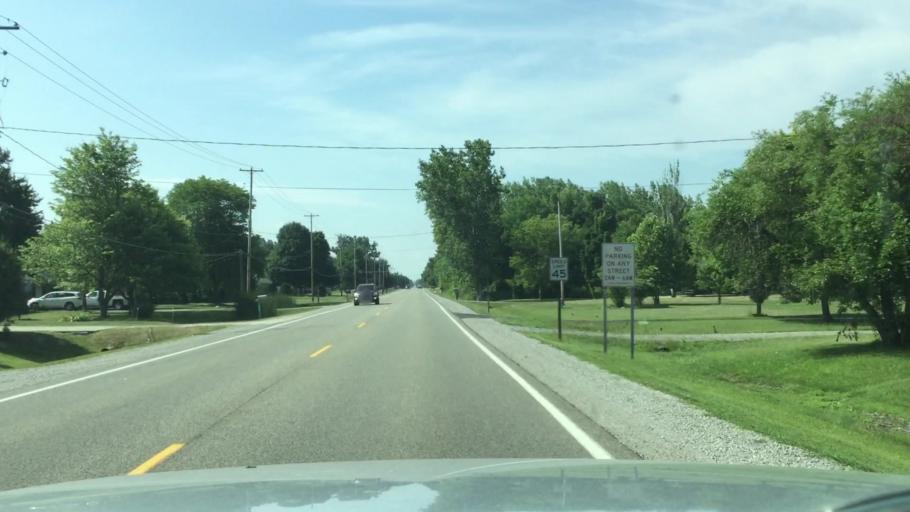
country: US
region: Michigan
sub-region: Genesee County
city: Flushing
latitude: 43.0745
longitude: -83.8134
